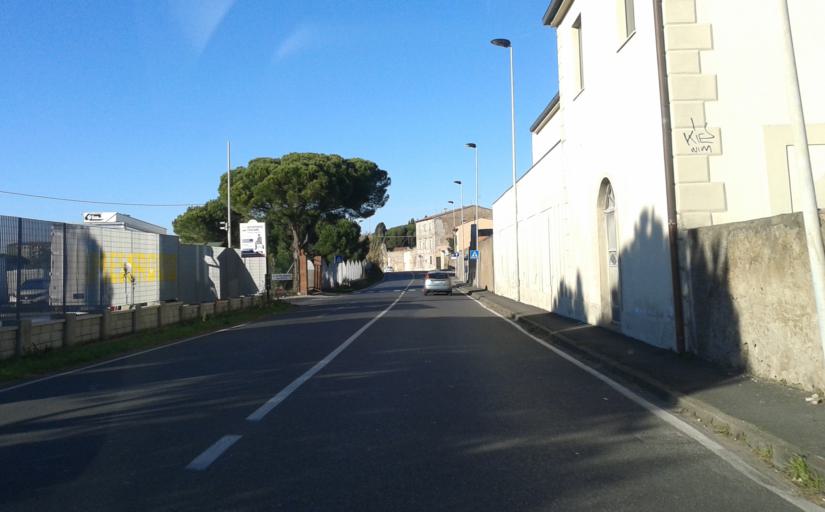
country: IT
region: Tuscany
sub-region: Provincia di Livorno
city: Livorno
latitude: 43.5287
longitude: 10.3214
